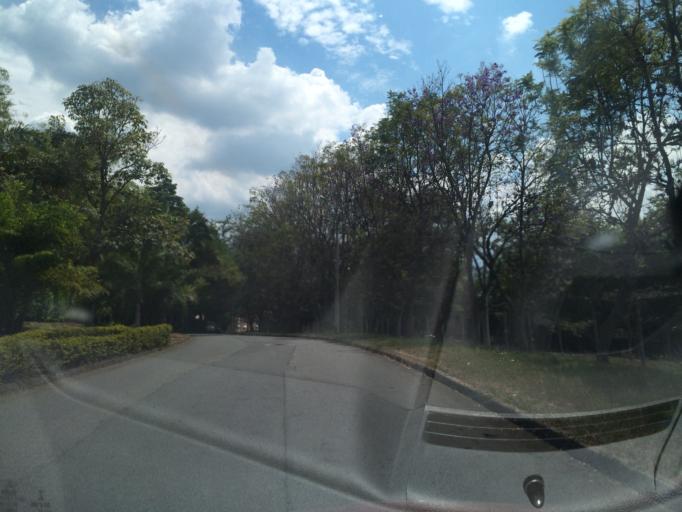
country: CO
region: Valle del Cauca
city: Jamundi
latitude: 3.3493
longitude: -76.5459
